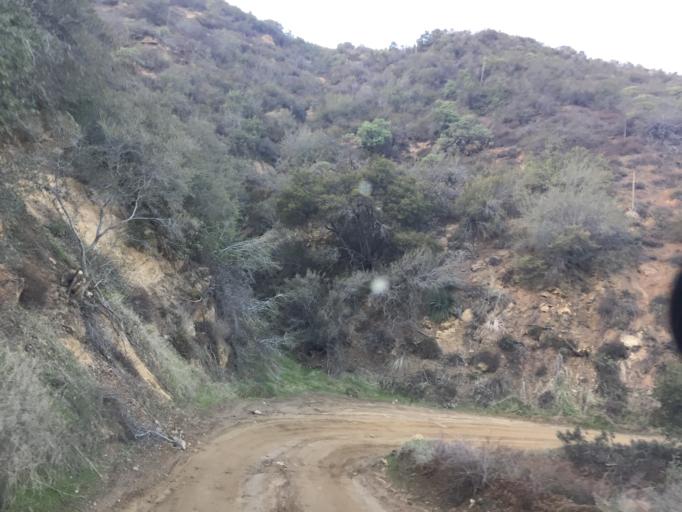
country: US
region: California
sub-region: San Bernardino County
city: Yucaipa
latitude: 34.1085
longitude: -117.0290
